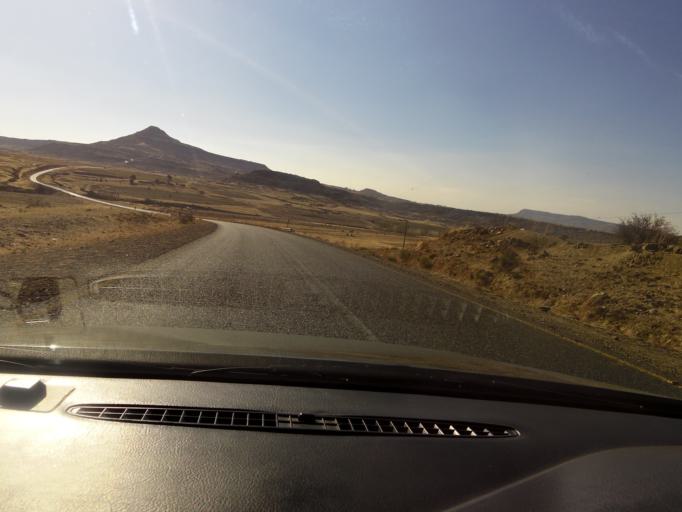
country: LS
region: Mohale's Hoek District
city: Mohale's Hoek
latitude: -30.0923
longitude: 27.4374
